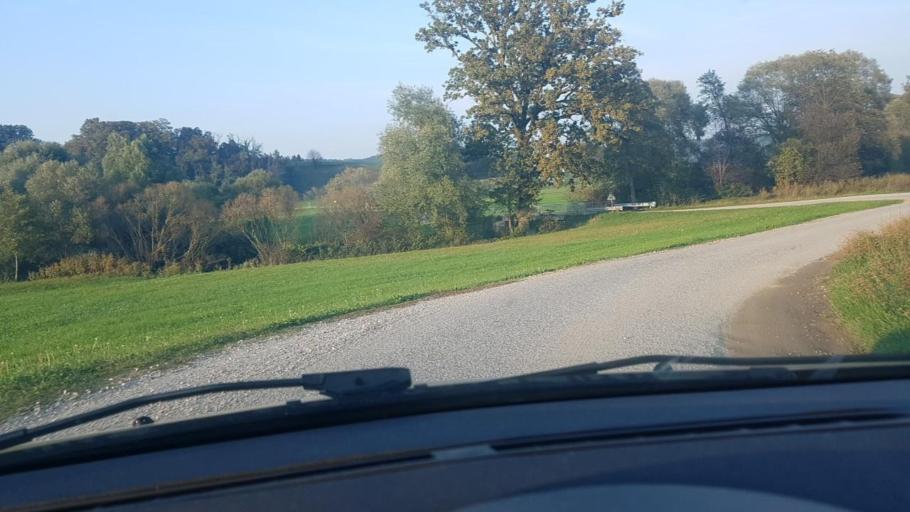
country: SI
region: Majsperk
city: Majsperk
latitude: 46.3363
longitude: 15.7181
